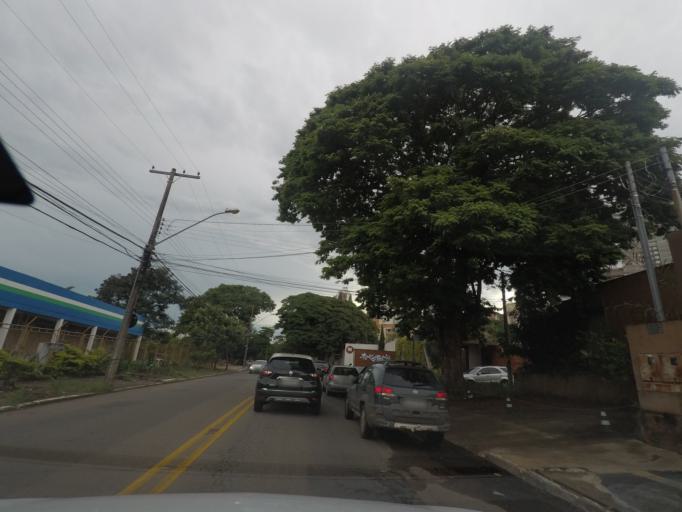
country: BR
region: Goias
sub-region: Goiania
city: Goiania
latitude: -16.7011
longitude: -49.2512
